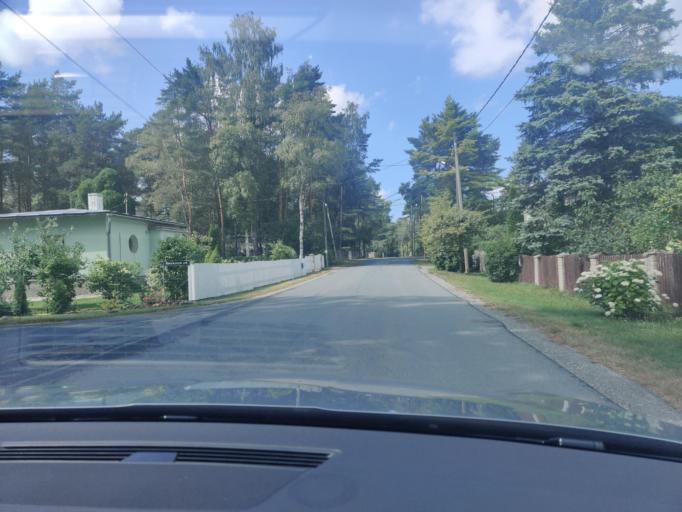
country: EE
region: Harju
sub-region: Saue vald
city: Laagri
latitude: 59.3555
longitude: 24.6211
